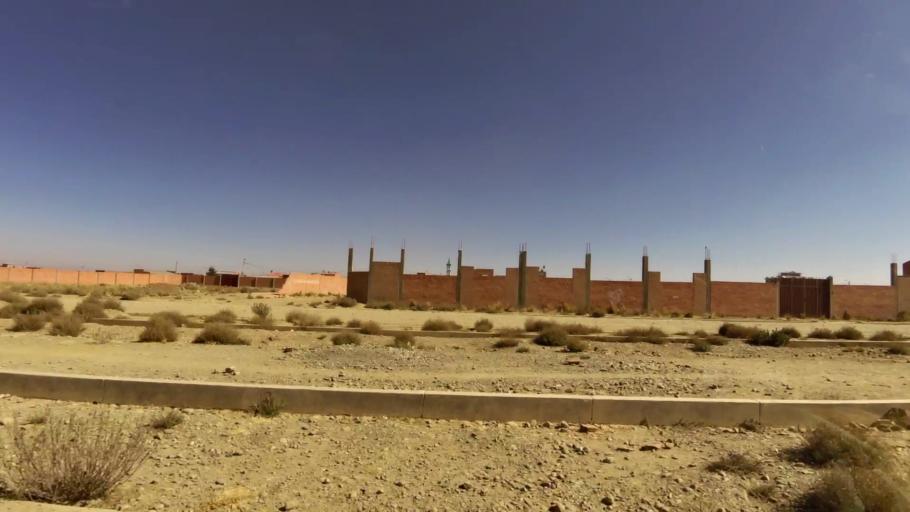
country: BO
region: La Paz
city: La Paz
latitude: -16.5969
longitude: -68.1990
